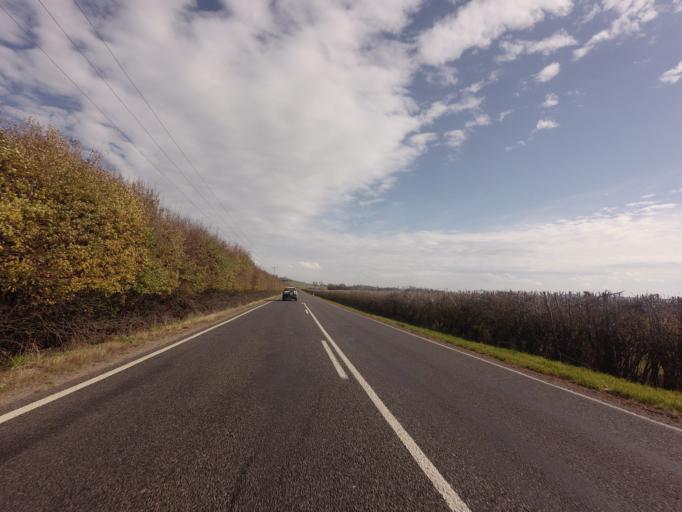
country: AU
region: Tasmania
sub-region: Meander Valley
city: Westbury
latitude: -41.5244
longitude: 146.7709
